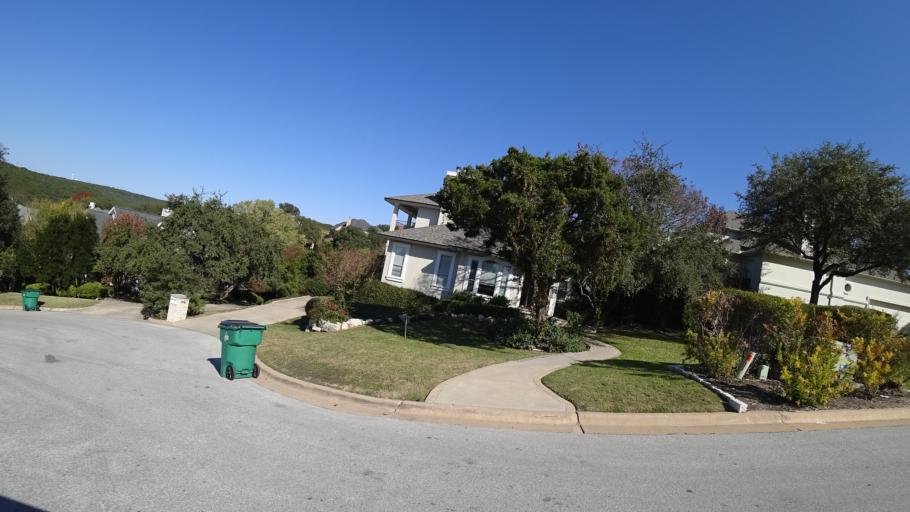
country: US
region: Texas
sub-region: Travis County
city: Lost Creek
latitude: 30.3698
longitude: -97.8632
